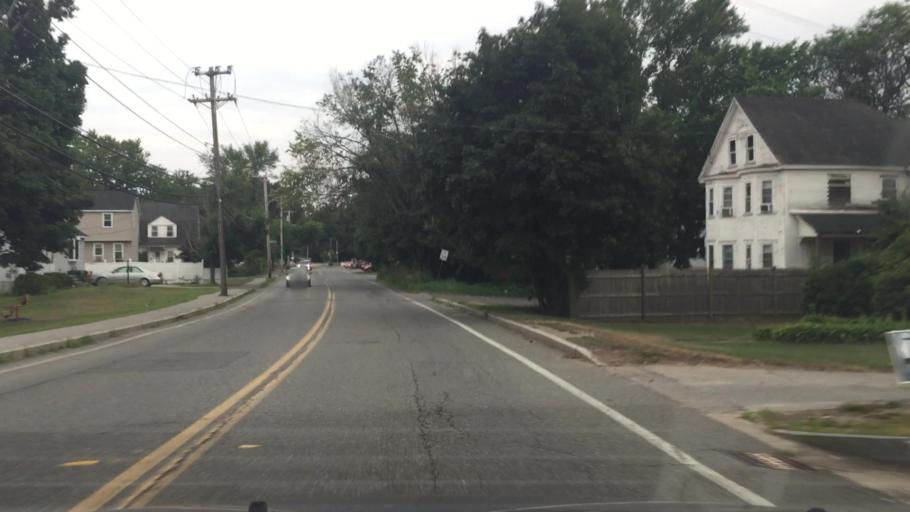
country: US
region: Massachusetts
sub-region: Middlesex County
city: Dracut
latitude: 42.6815
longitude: -71.3540
